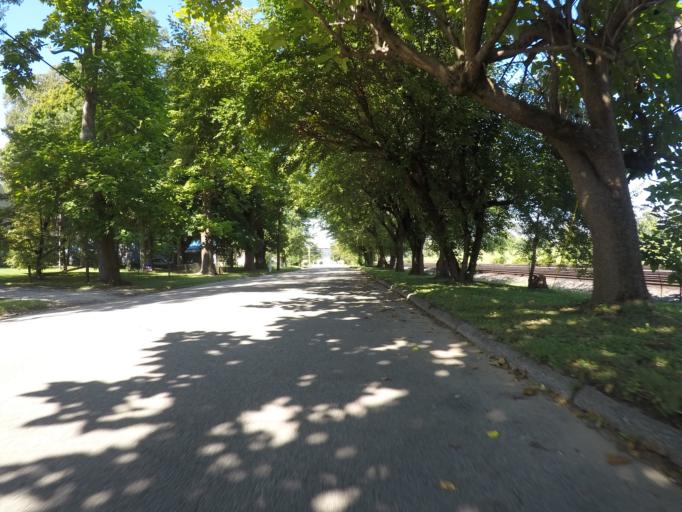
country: US
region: West Virginia
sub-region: Wayne County
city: Kenova
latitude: 38.4013
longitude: -82.5712
